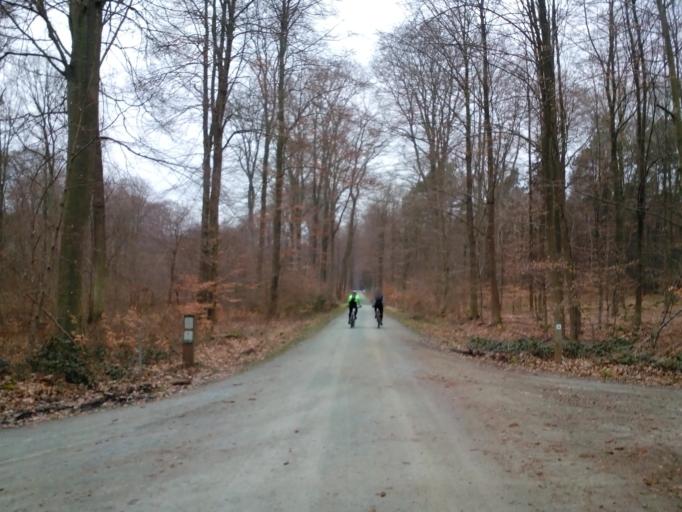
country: BE
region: Flanders
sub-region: Provincie Vlaams-Brabant
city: Bierbeek
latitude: 50.8086
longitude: 4.7131
